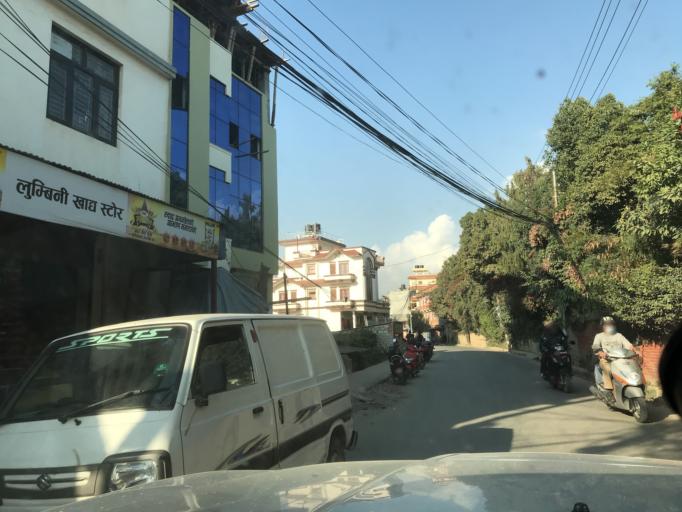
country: NP
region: Central Region
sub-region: Bagmati Zone
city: Patan
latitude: 27.6592
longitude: 85.3170
